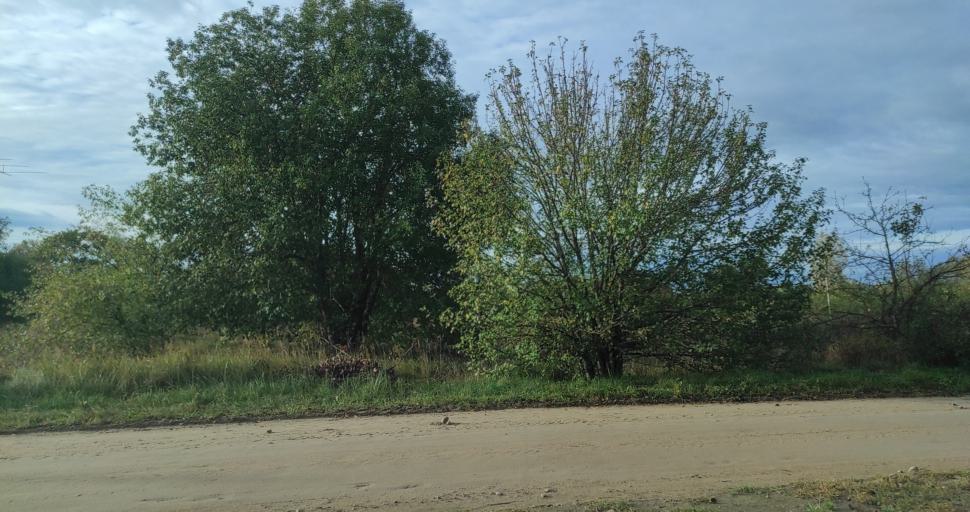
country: LV
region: Aizpute
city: Aizpute
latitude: 56.8050
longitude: 21.6634
